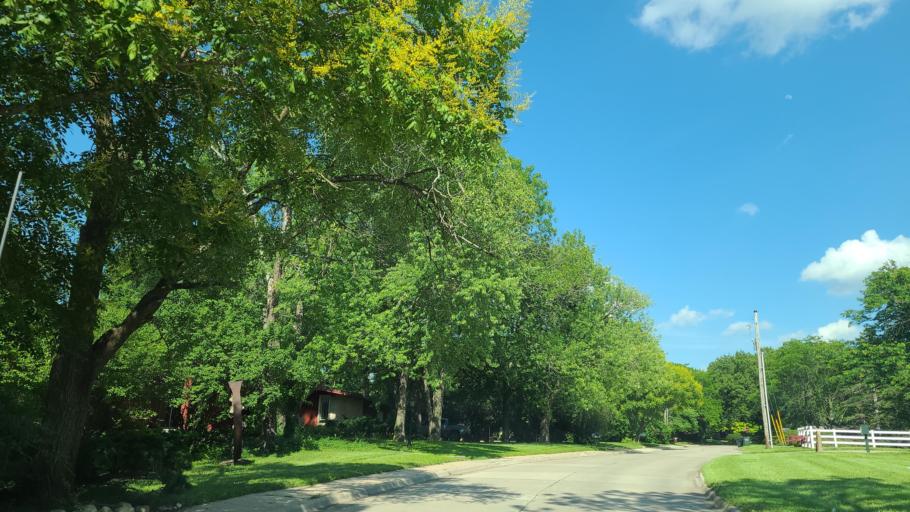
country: US
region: Kansas
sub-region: Douglas County
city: Lawrence
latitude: 38.9631
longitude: -95.2657
